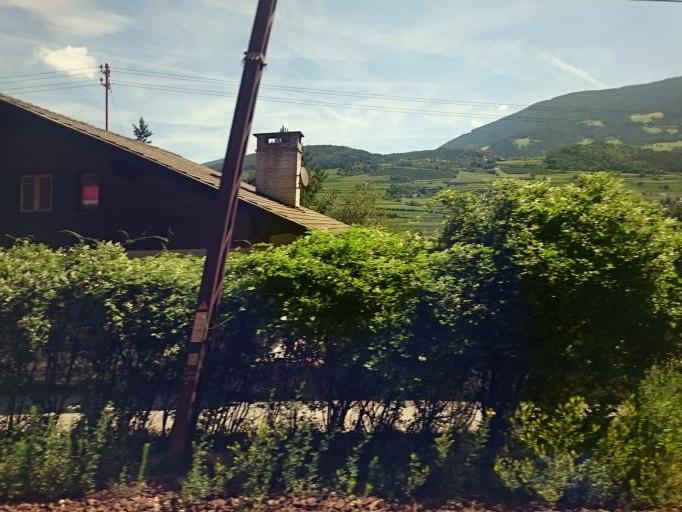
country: IT
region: Trentino-Alto Adige
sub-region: Bolzano
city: Leone-Santa Elisabetta
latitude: 46.7287
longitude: 11.6423
